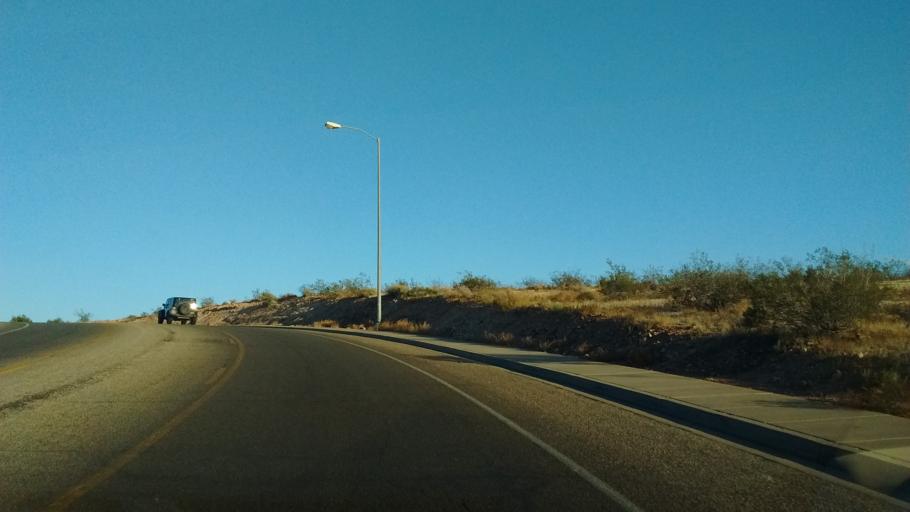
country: US
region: Utah
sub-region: Washington County
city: Saint George
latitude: 37.0927
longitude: -113.5498
